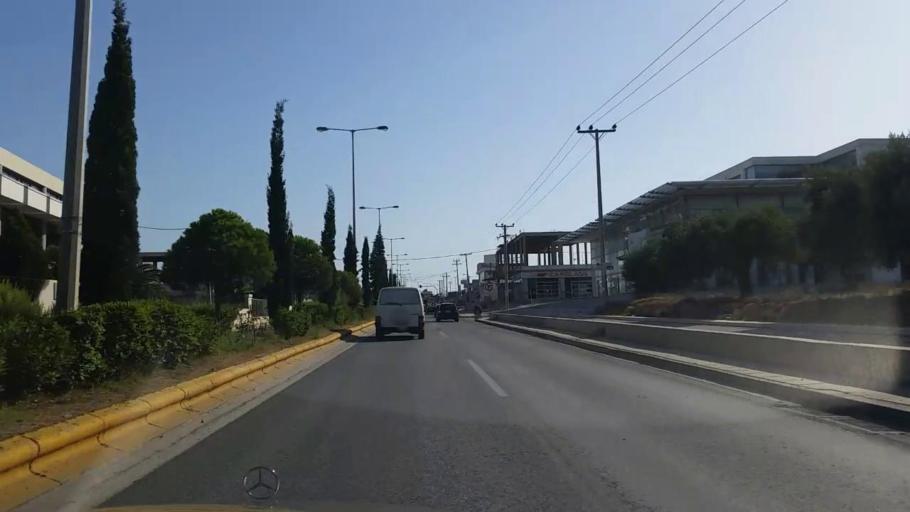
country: GR
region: Attica
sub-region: Nomarchia Anatolikis Attikis
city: Koropi
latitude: 37.8842
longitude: 23.8766
